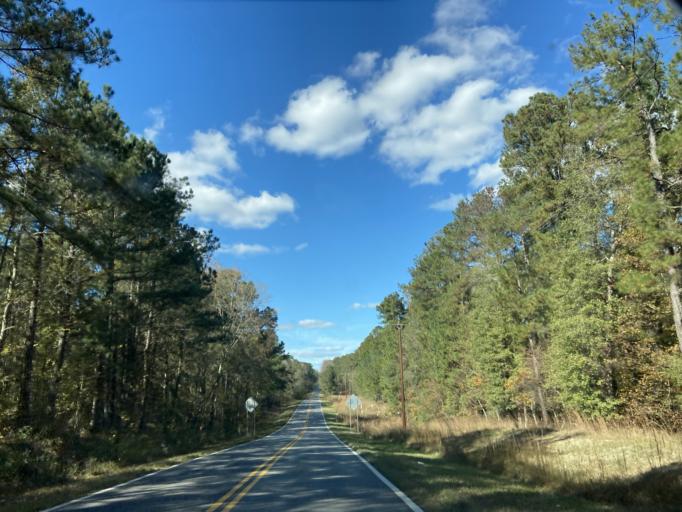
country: US
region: Georgia
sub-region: Jones County
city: Gray
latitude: 32.9316
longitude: -83.5027
